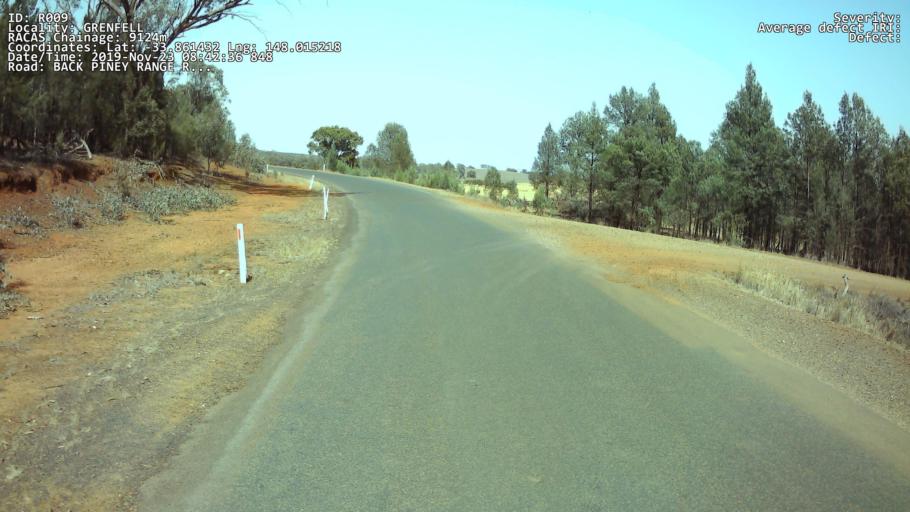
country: AU
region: New South Wales
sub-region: Weddin
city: Grenfell
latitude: -33.8614
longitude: 148.0152
